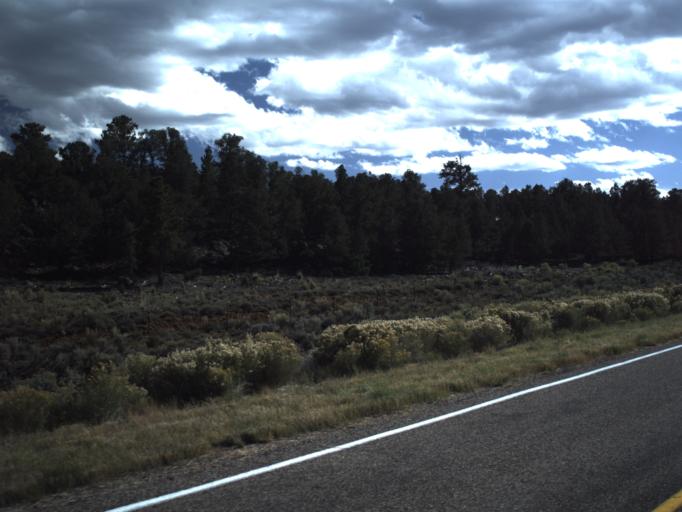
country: US
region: Utah
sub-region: Garfield County
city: Panguitch
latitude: 37.7766
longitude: -112.4429
